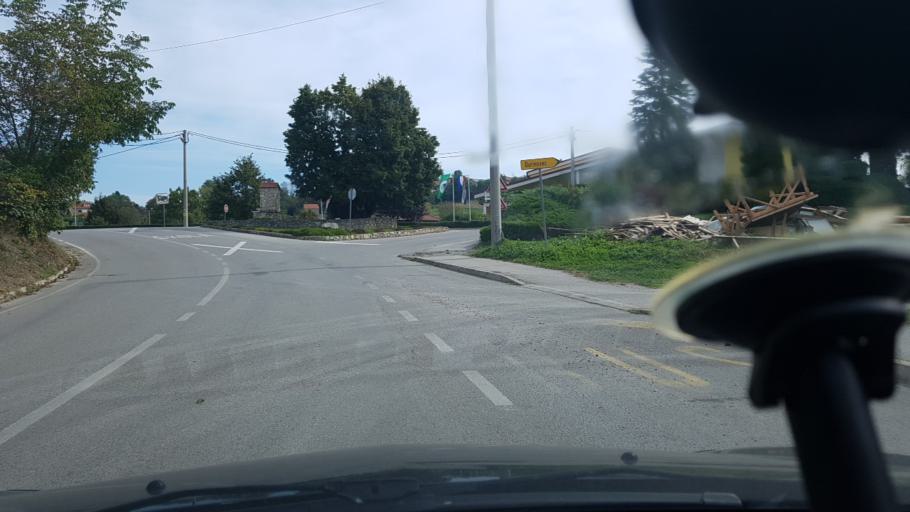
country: HR
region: Varazdinska
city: Remetinec
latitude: 46.0886
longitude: 16.3228
